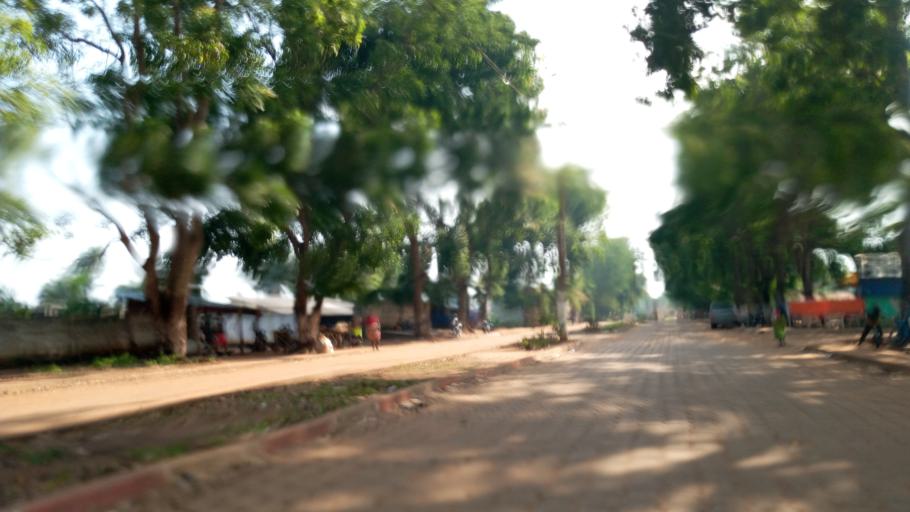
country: BJ
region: Queme
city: Porto-Novo
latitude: 6.5550
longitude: 2.6600
